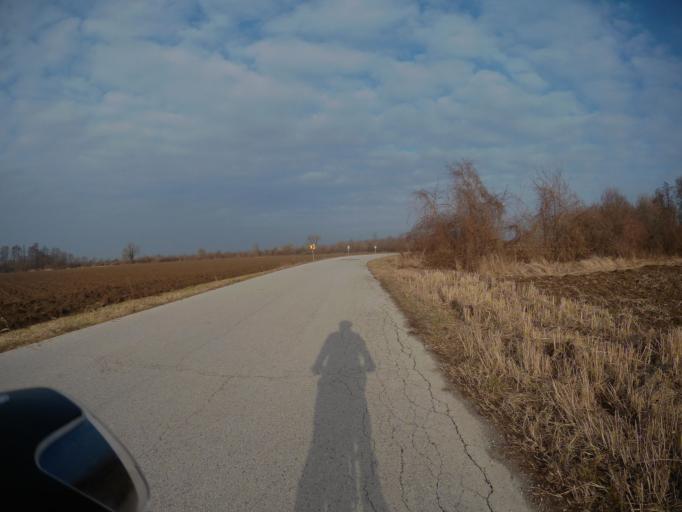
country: HR
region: Zagrebacka
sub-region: Grad Velika Gorica
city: Velika Gorica
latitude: 45.7226
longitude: 16.1172
